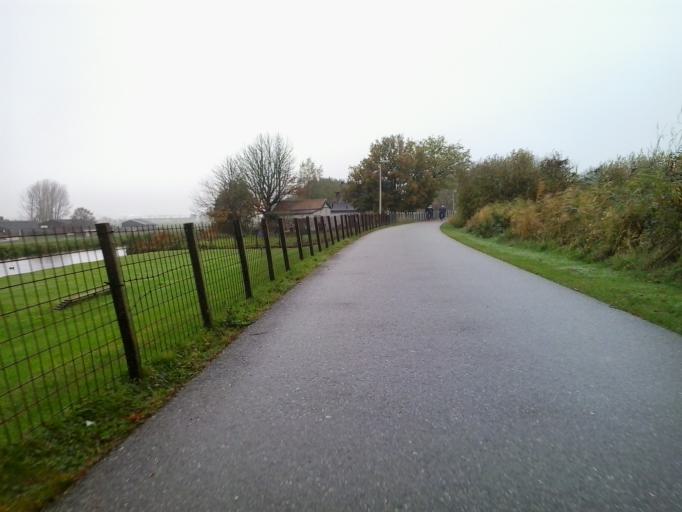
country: NL
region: South Holland
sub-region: Gemeente Lansingerland
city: Bleiswijk
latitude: 51.9821
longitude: 4.5490
